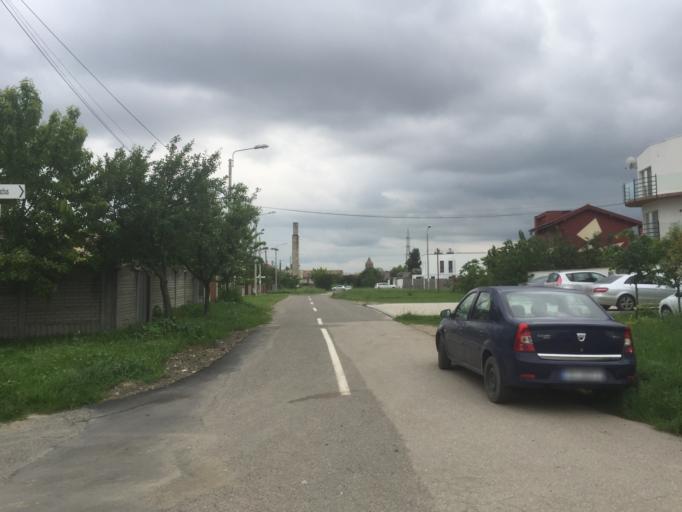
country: RO
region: Timis
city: Timisoara
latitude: 45.7549
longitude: 21.1973
